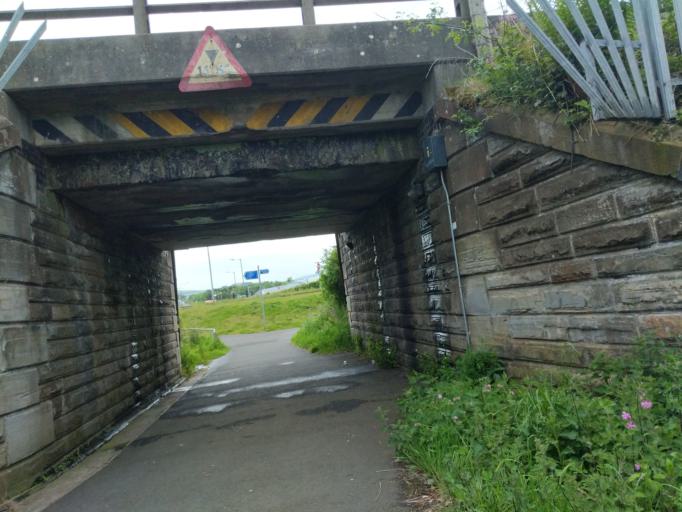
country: GB
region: Scotland
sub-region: Edinburgh
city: Currie
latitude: 55.9278
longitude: -3.3060
